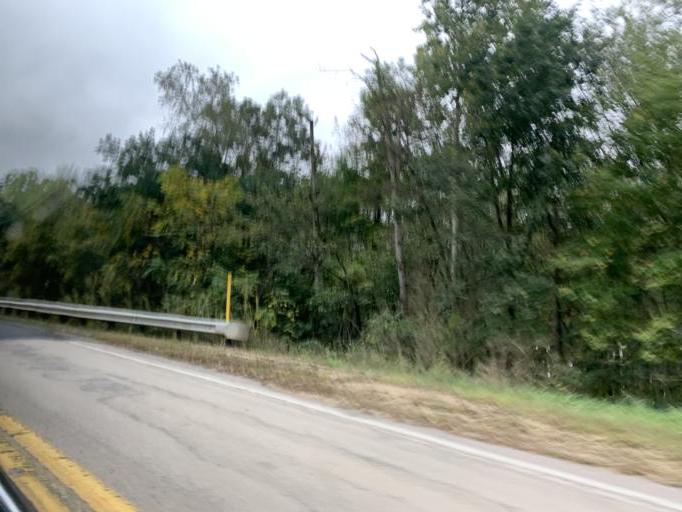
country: US
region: Wisconsin
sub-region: Grant County
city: Muscoda
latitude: 43.2024
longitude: -90.4379
